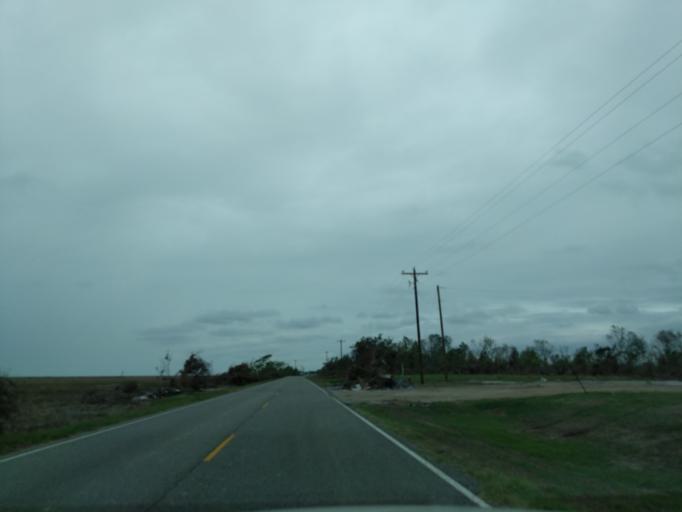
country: US
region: Louisiana
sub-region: Cameron Parish
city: Cameron
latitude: 29.7869
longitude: -93.1397
